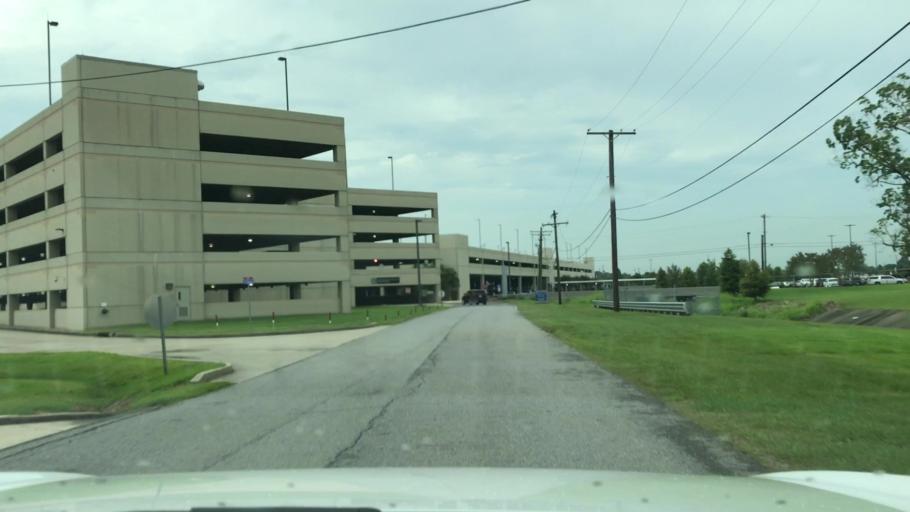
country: US
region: Louisiana
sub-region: East Baton Rouge Parish
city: Brownsfield
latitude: 30.5354
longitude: -91.1586
